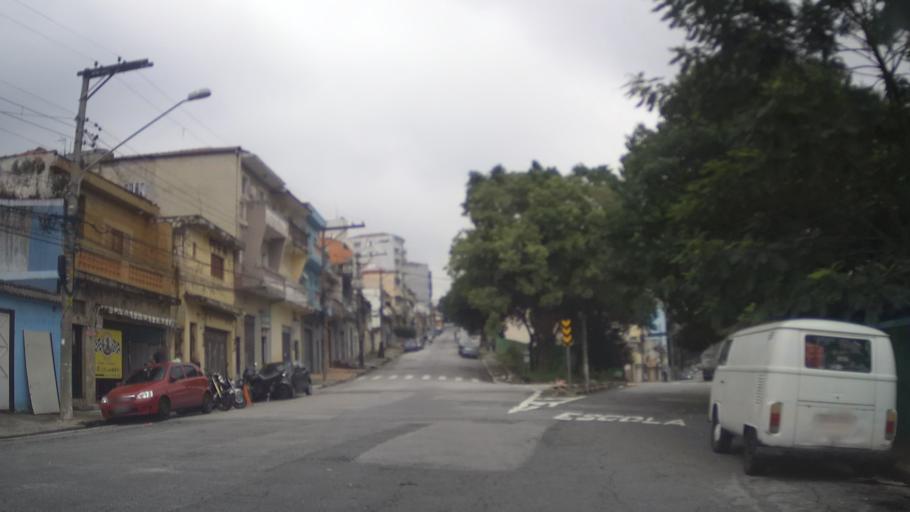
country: BR
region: Sao Paulo
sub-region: Sao Paulo
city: Sao Paulo
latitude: -23.5066
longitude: -46.5862
